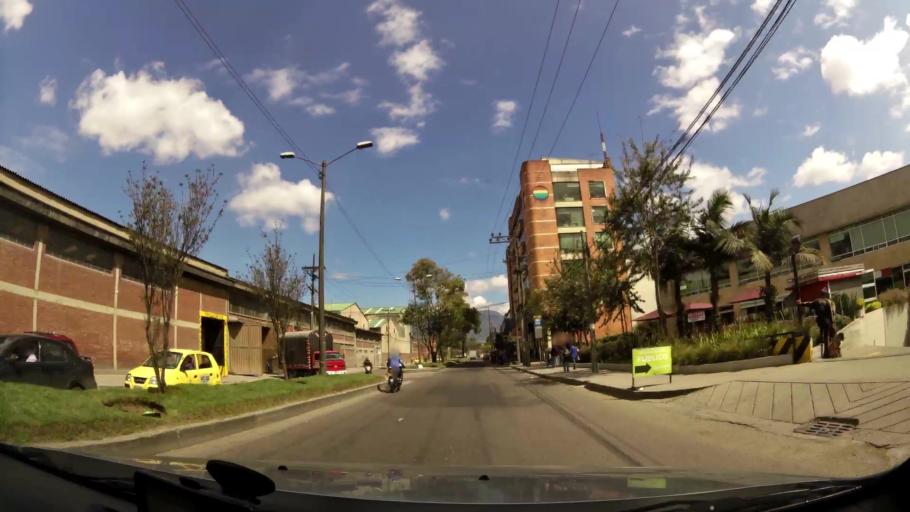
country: CO
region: Bogota D.C.
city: Bogota
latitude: 4.6392
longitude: -74.1150
